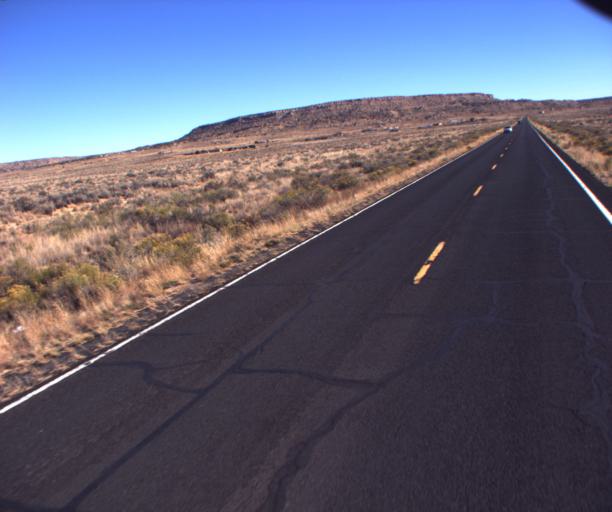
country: US
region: Arizona
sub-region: Navajo County
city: First Mesa
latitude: 35.8412
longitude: -110.3205
